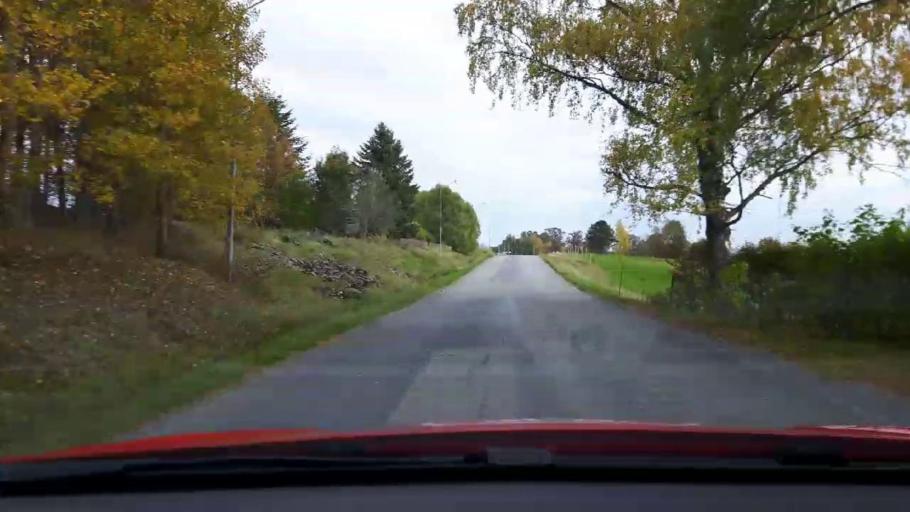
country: SE
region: Jaemtland
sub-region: Krokoms Kommun
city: Valla
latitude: 63.2538
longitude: 14.0279
